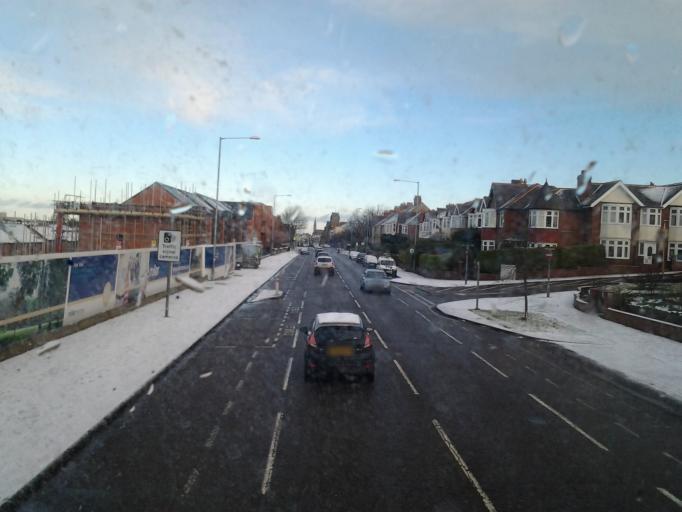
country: GB
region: England
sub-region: Gateshead
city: Gateshead
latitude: 54.9459
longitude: -1.5997
